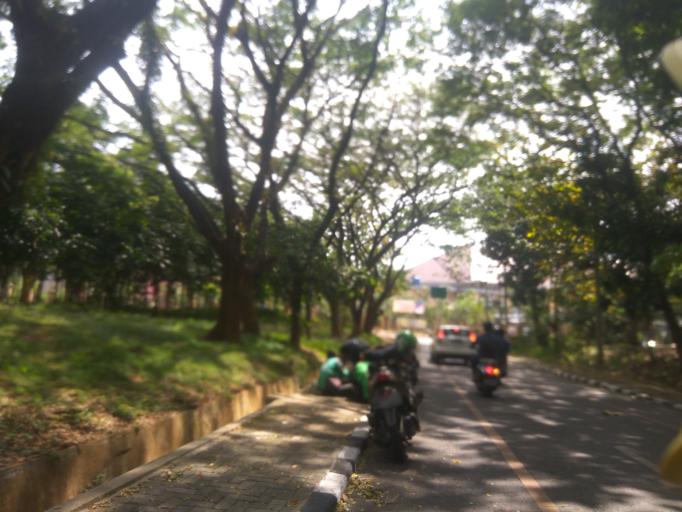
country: ID
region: Central Java
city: Semarang
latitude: -7.0482
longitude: 110.4404
